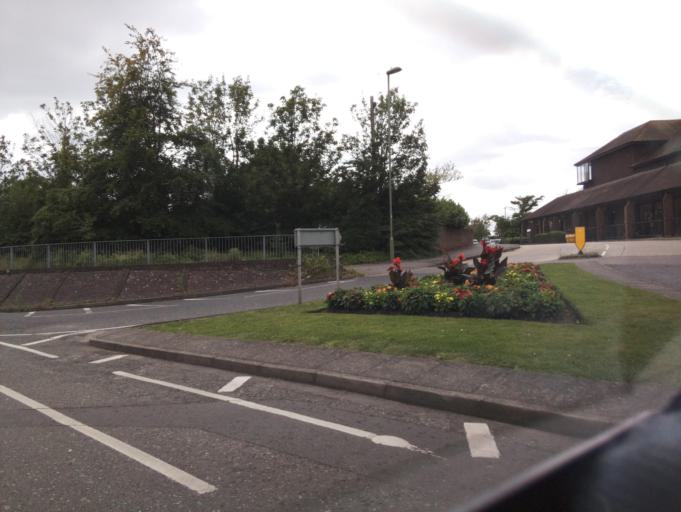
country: GB
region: England
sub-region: Hampshire
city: Lymington
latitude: 50.7573
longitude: -1.5496
